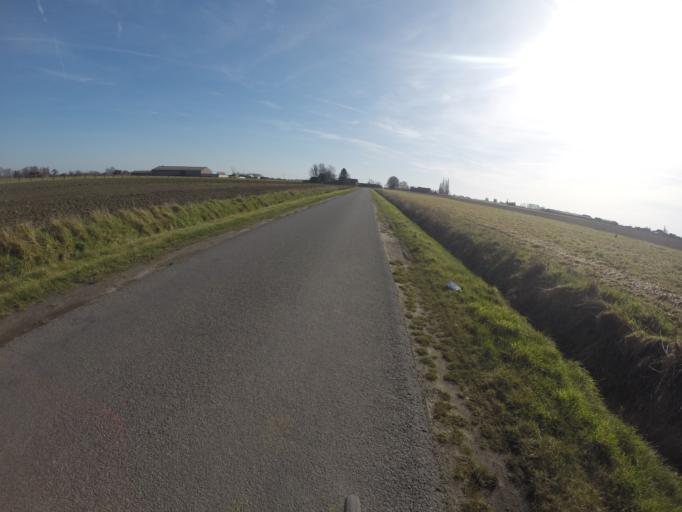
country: BE
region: Flanders
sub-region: Provincie West-Vlaanderen
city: Wingene
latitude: 51.0653
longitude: 3.3336
